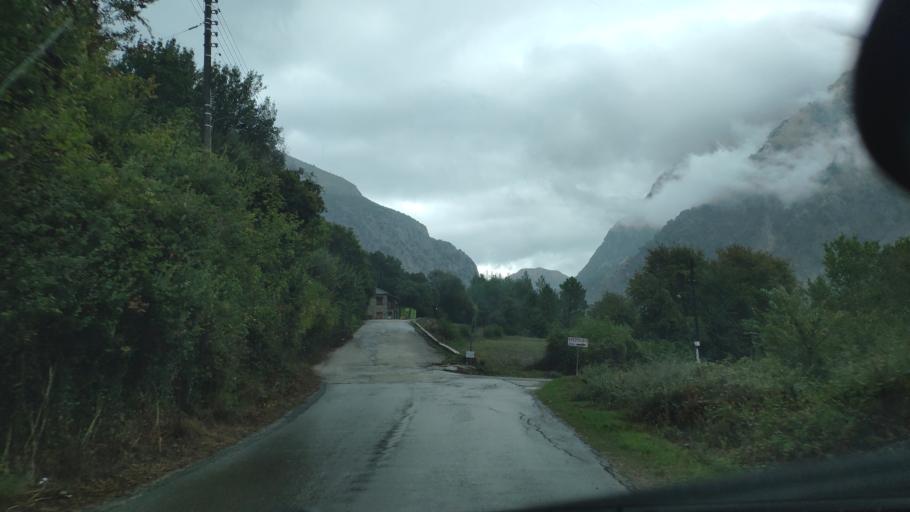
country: GR
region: West Greece
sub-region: Nomos Aitolias kai Akarnanias
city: Krikellos
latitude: 39.0264
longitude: 21.3178
